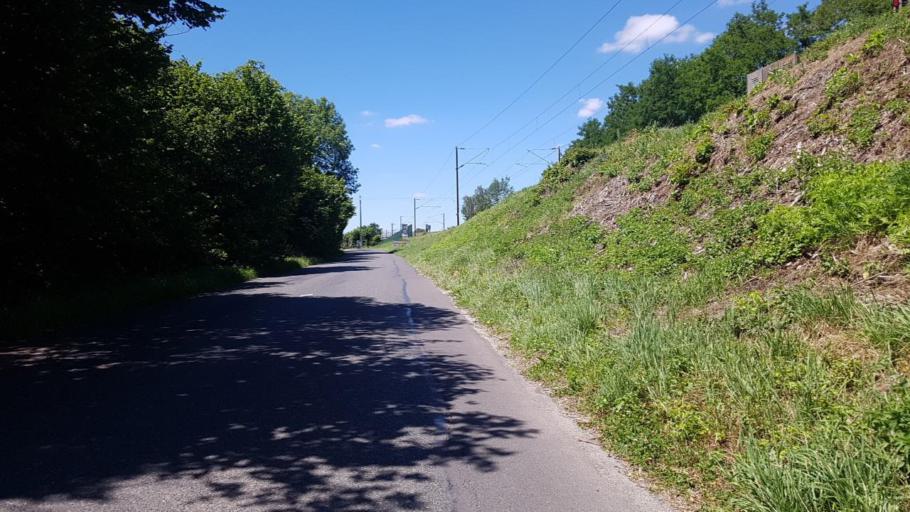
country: FR
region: Ile-de-France
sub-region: Departement de Seine-et-Marne
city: Changis-sur-Marne
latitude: 48.9591
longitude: 3.0331
